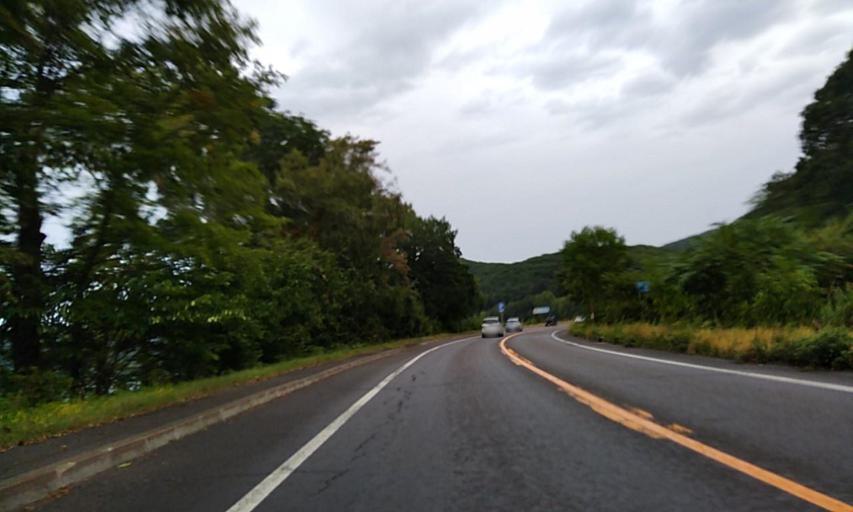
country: JP
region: Hokkaido
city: Abashiri
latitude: 43.9913
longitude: 144.2193
